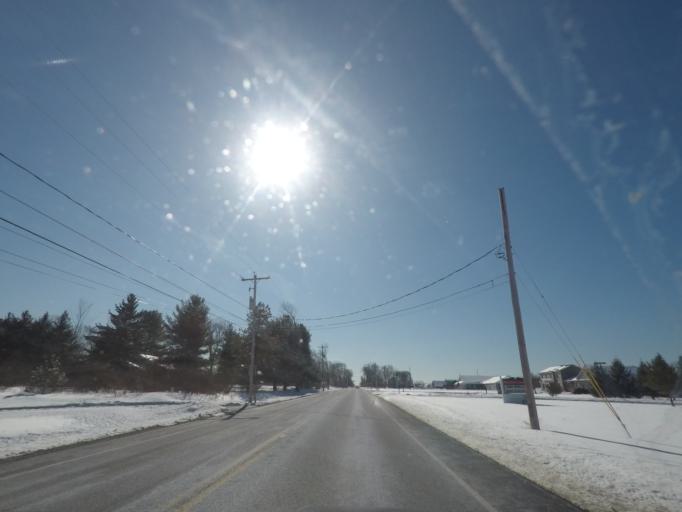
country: US
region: New York
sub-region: Saratoga County
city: Ballston Spa
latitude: 42.9629
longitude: -73.8296
